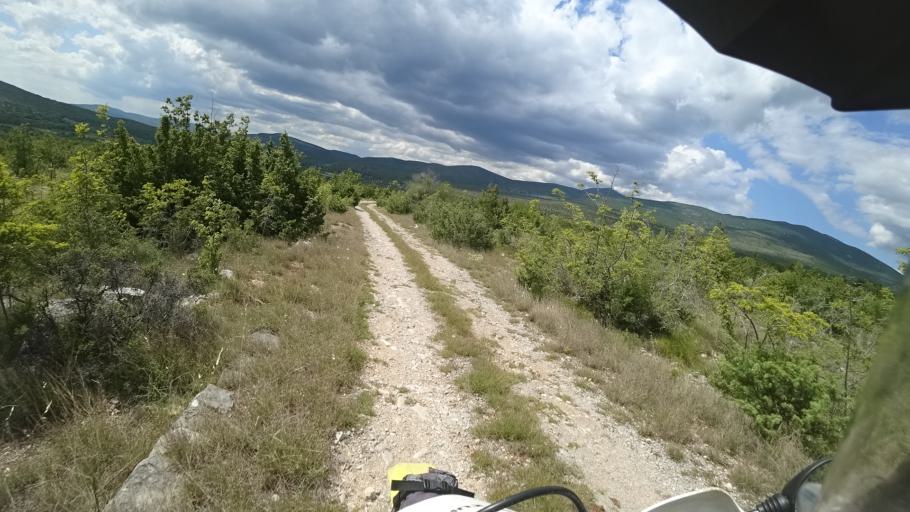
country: HR
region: Sibensko-Kniniska
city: Kistanje
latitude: 44.0892
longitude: 16.0484
